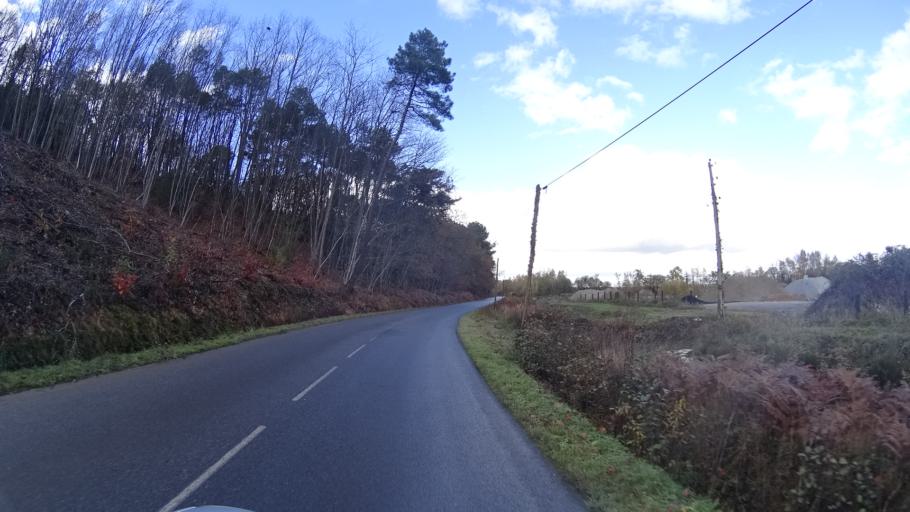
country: FR
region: Brittany
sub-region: Departement du Morbihan
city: Saint-Jean-la-Poterie
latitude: 47.6374
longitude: -2.1092
